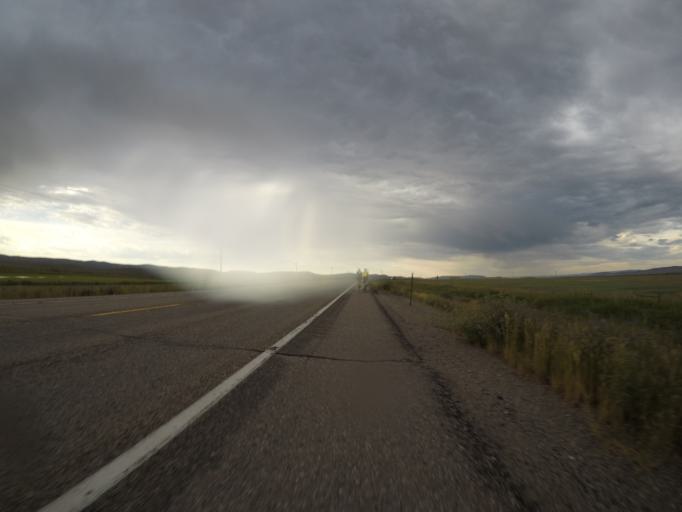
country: US
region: Utah
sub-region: Rich County
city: Randolph
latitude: 41.9399
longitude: -110.9529
